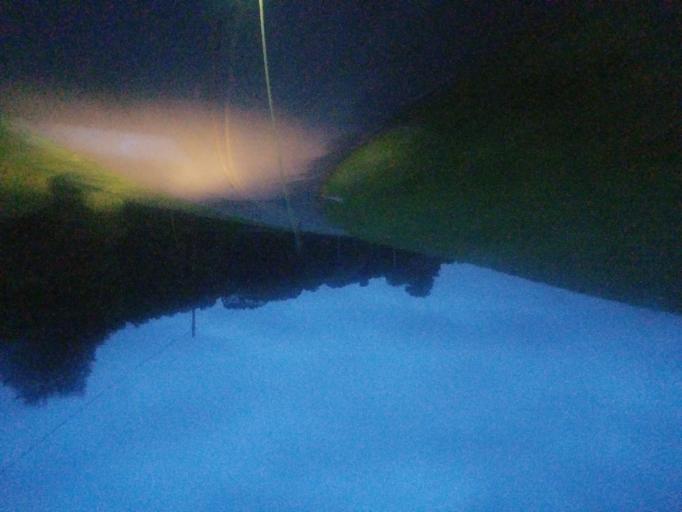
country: US
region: Ohio
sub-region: Carroll County
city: Carrollton
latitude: 40.6118
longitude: -80.9919
